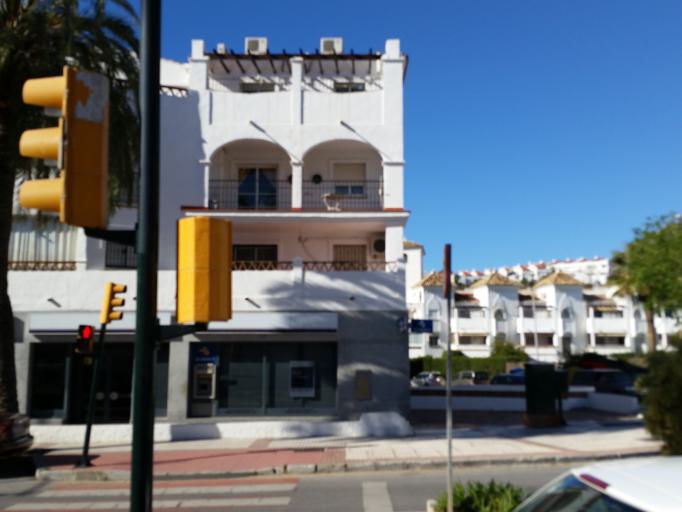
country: ES
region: Andalusia
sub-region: Provincia de Malaga
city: Benalmadena
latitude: 36.5900
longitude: -4.5336
